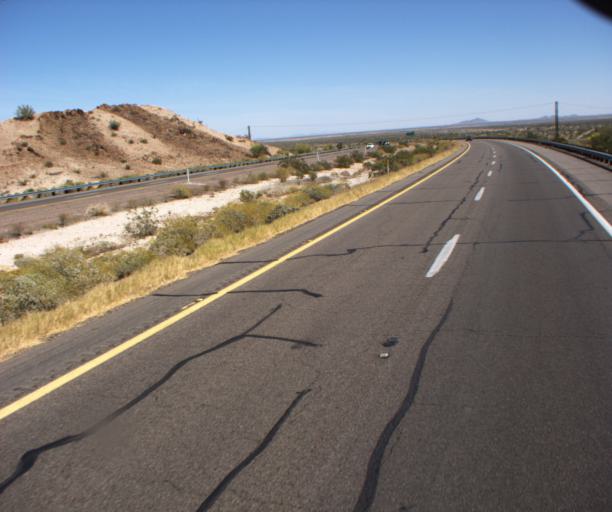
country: US
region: Arizona
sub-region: Yuma County
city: Wellton
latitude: 32.7260
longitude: -113.7424
